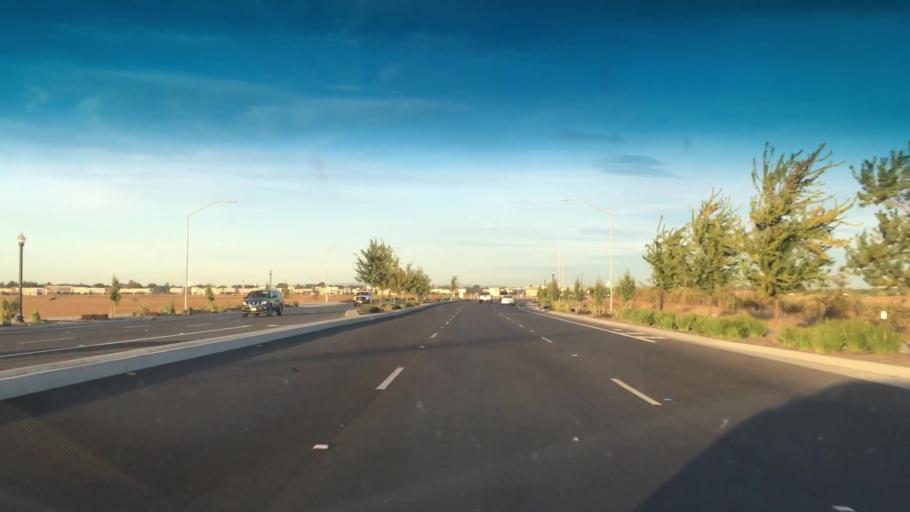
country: US
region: California
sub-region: Sacramento County
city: Parkway
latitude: 38.4642
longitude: -121.4793
